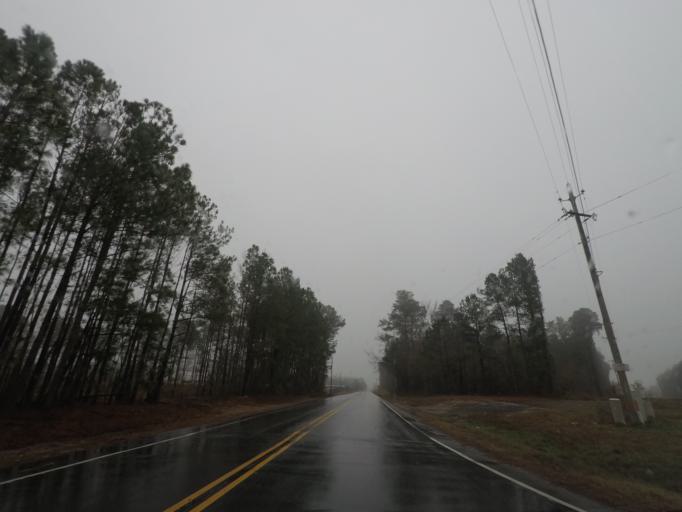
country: US
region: North Carolina
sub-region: Scotland County
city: Laurinburg
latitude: 34.8233
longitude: -79.4588
